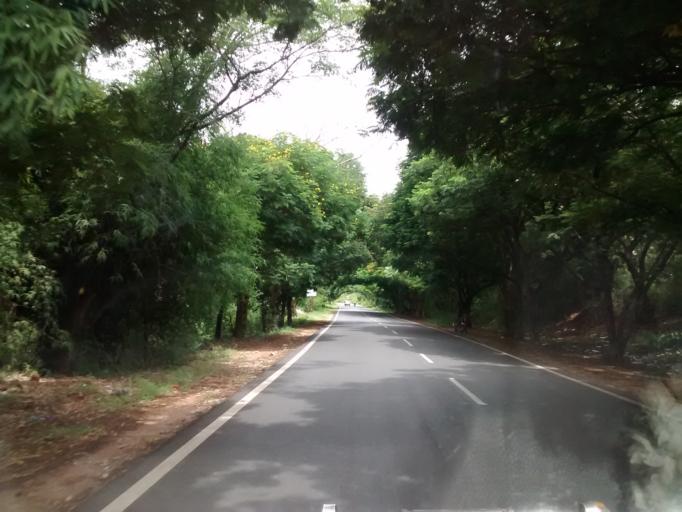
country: IN
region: Andhra Pradesh
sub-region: Chittoor
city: Tirupati
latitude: 13.6272
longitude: 79.3705
